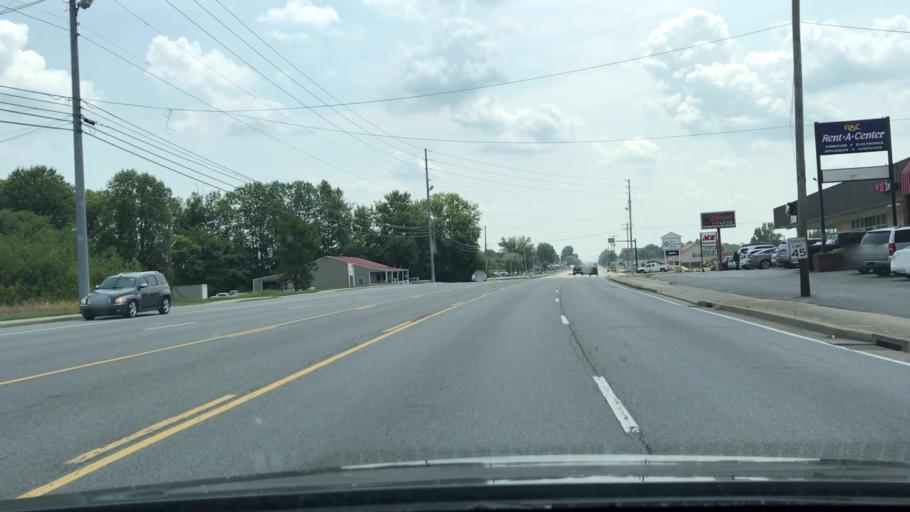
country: US
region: Tennessee
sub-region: Sumner County
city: Portland
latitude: 36.5748
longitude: -86.5137
